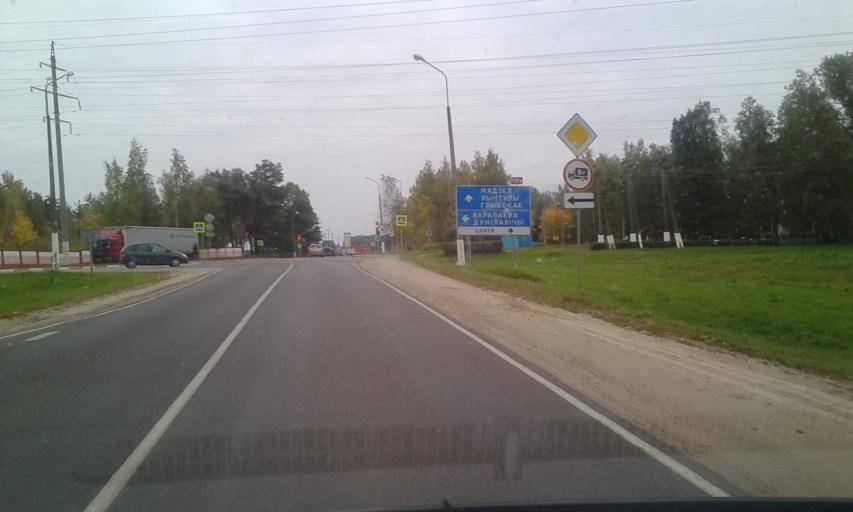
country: BY
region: Vitebsk
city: Pastavy
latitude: 55.1139
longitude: 26.8724
